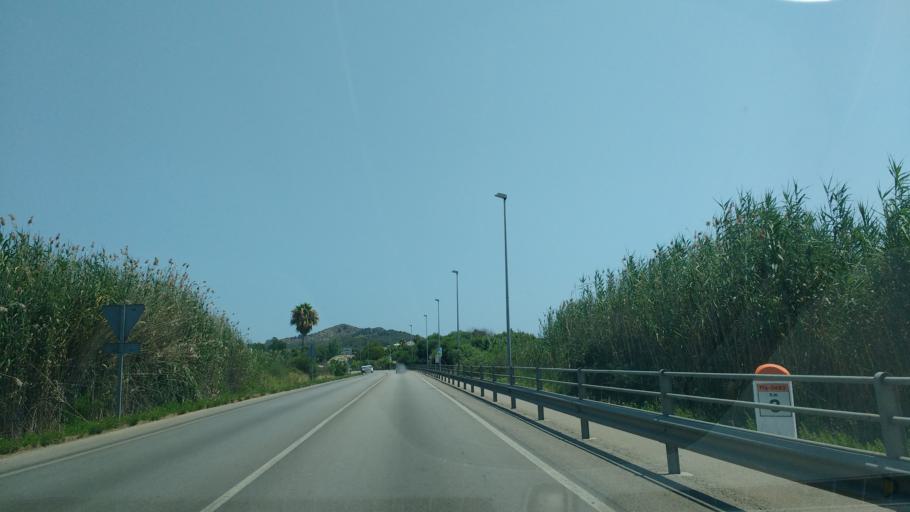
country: ES
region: Balearic Islands
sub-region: Illes Balears
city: Port d'Alcudia
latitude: 39.8460
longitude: 3.1267
